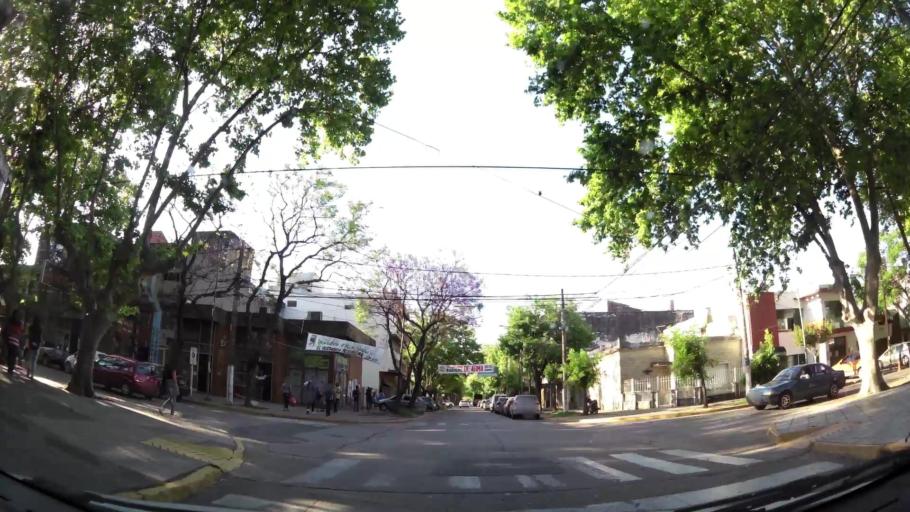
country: AR
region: Buenos Aires
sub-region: Partido de Merlo
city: Merlo
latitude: -34.6698
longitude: -58.7243
